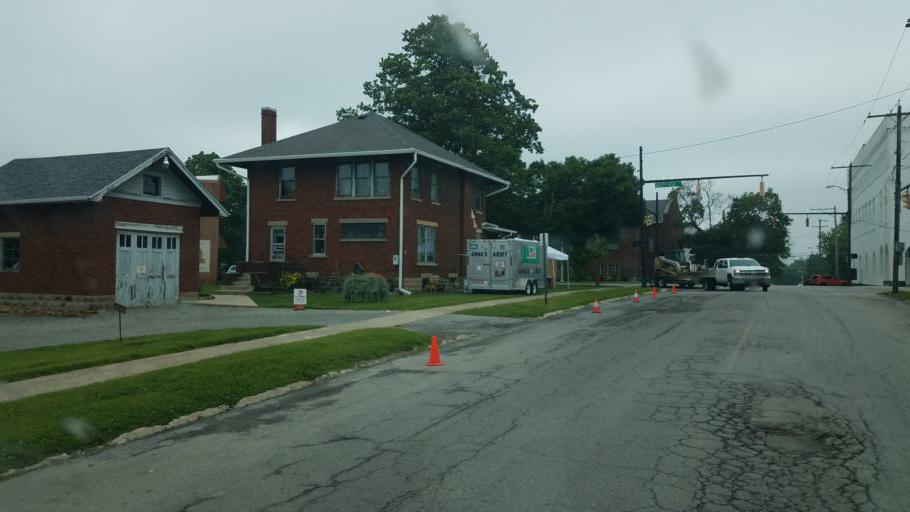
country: US
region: Ohio
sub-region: Highland County
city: Hillsboro
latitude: 39.2036
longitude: -83.6119
